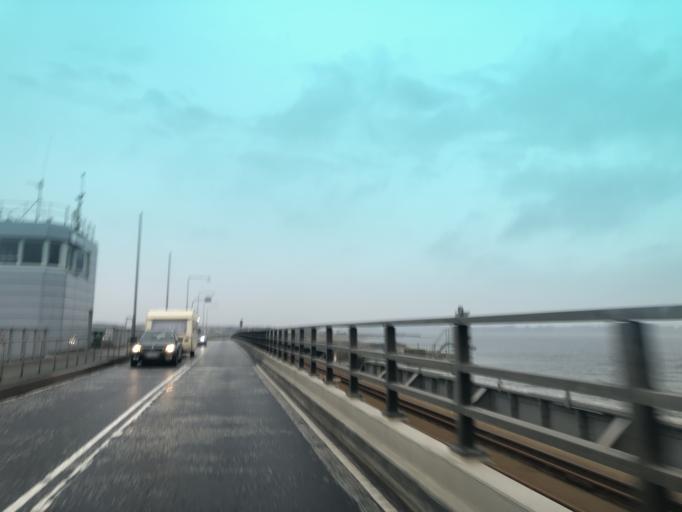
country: DK
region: Central Jutland
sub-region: Struer Kommune
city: Struer
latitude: 56.5785
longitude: 8.5579
